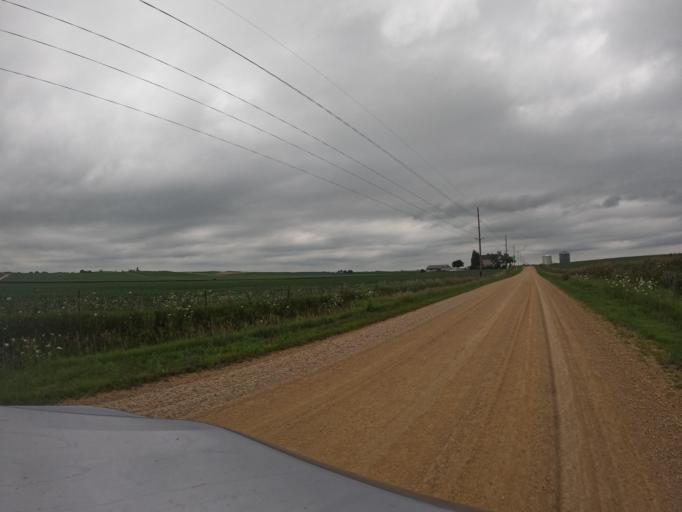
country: US
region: Iowa
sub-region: Clinton County
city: De Witt
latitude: 41.9392
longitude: -90.5872
